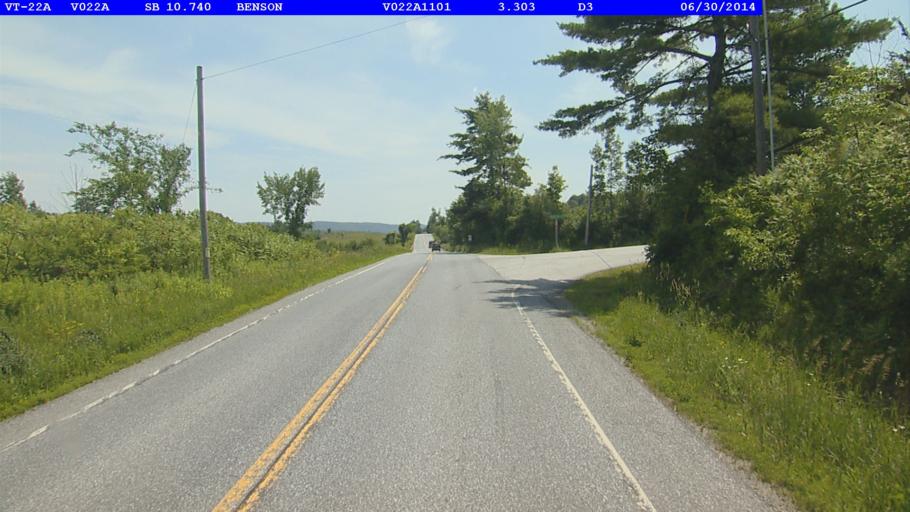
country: US
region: Vermont
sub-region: Rutland County
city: Fair Haven
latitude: 43.7159
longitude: -73.2987
